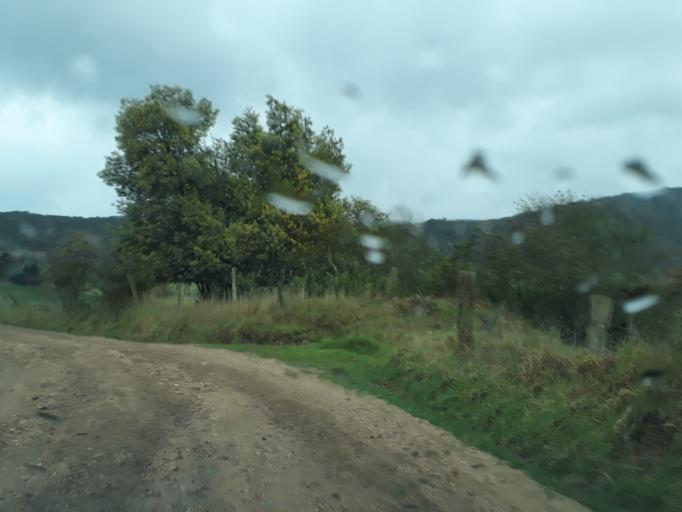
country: CO
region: Cundinamarca
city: Lenguazaque
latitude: 5.2782
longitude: -73.6476
